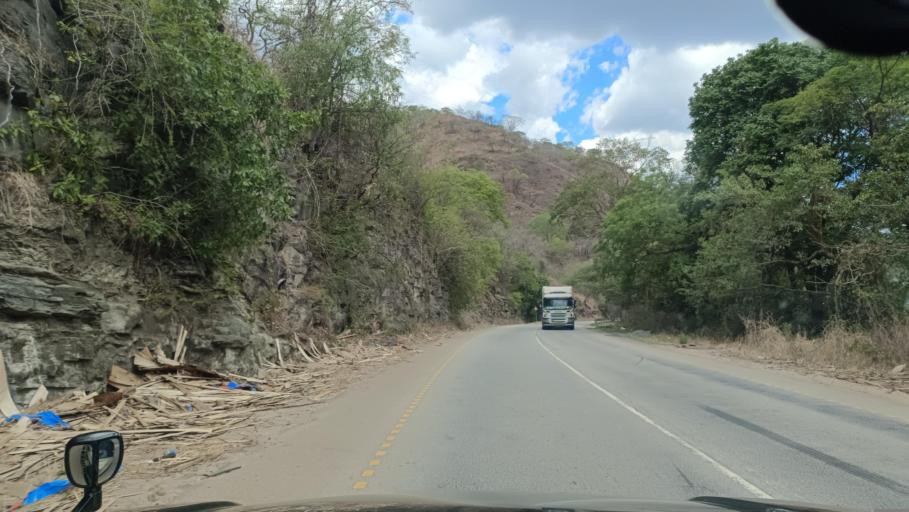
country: TZ
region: Morogoro
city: Kidatu
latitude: -7.5754
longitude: 36.7543
